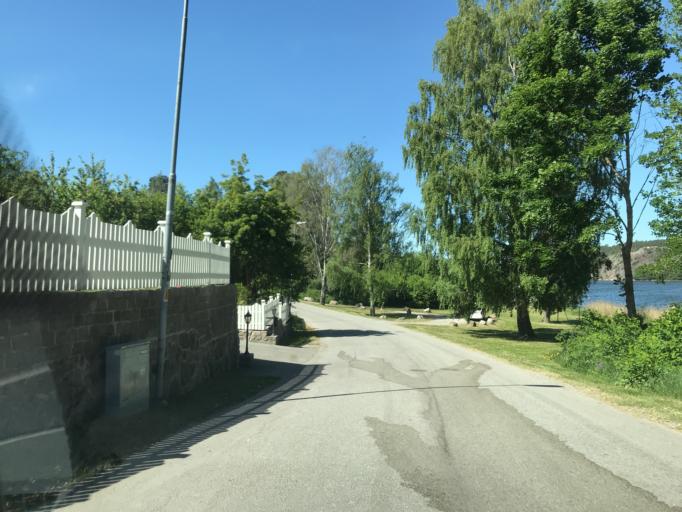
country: SE
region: Stockholm
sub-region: Sollentuna Kommun
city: Sollentuna
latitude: 59.4221
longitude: 17.9778
